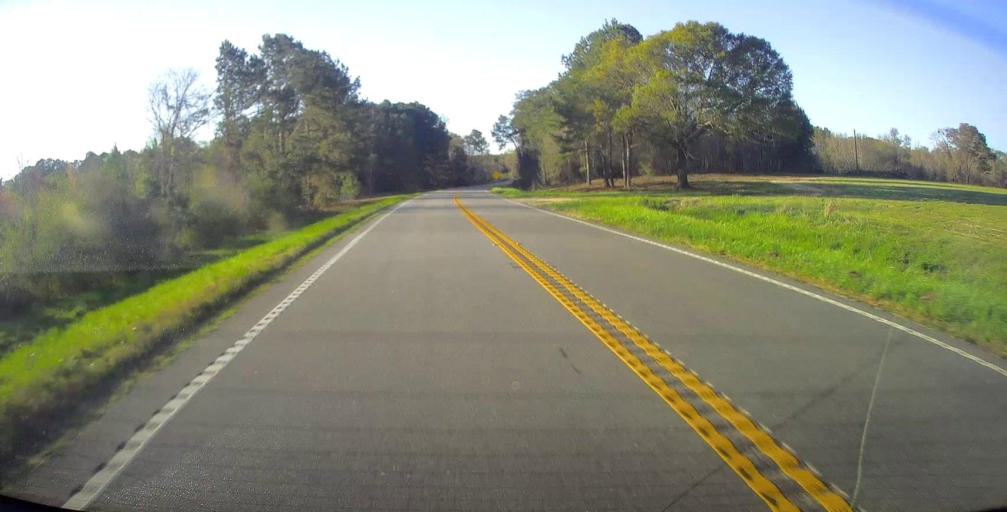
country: US
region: Georgia
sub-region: Pulaski County
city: Hawkinsville
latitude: 32.1895
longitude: -83.3677
